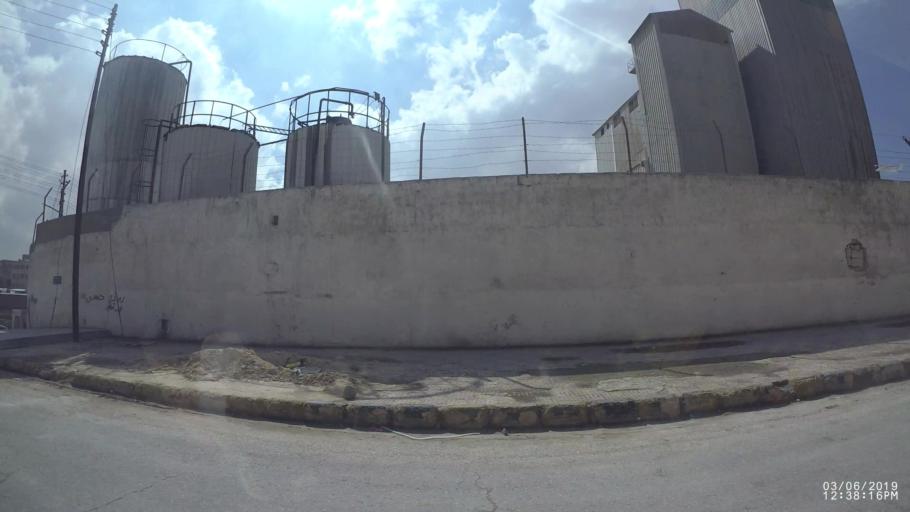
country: JO
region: Zarqa
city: Russeifa
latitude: 31.9884
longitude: 35.9963
